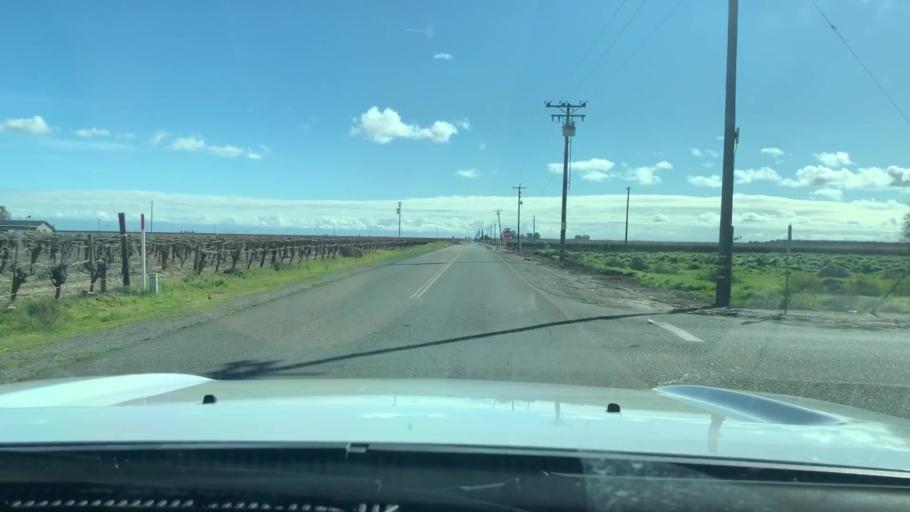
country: US
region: California
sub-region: Fresno County
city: Laton
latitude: 36.4893
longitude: -119.6899
